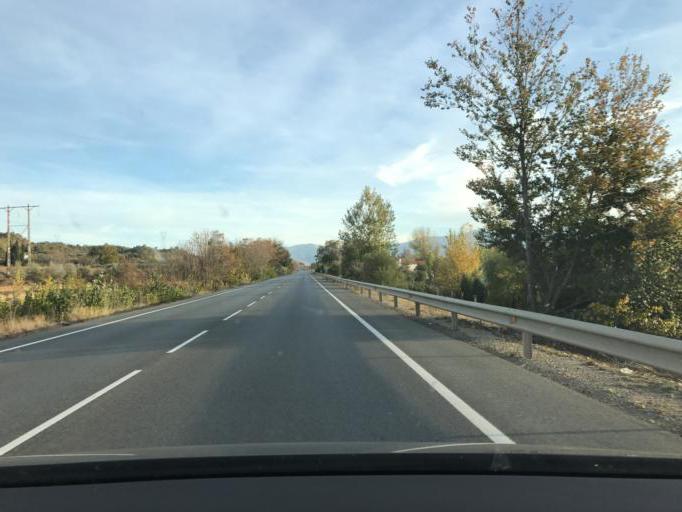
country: ES
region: Andalusia
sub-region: Provincia de Granada
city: Guadix
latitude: 37.2812
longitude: -3.1140
